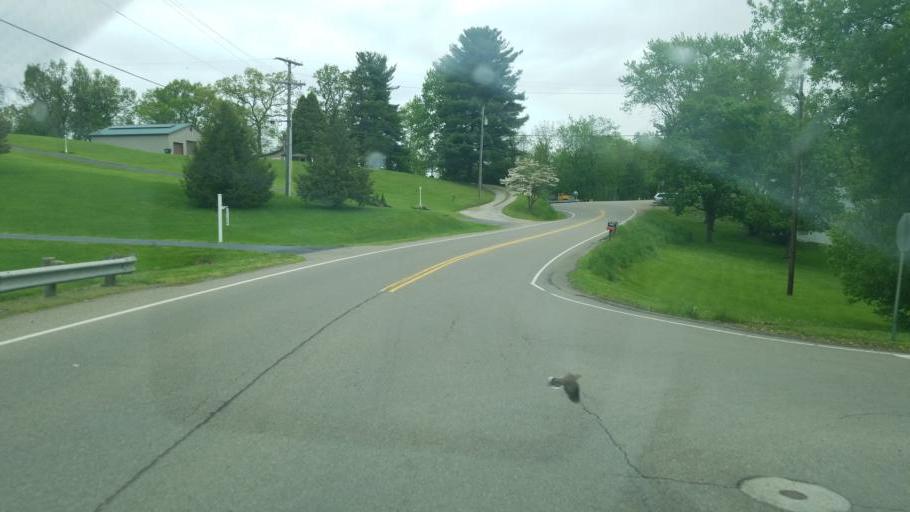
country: US
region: Ohio
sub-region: Coshocton County
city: Coshocton
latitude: 40.2527
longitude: -81.8321
